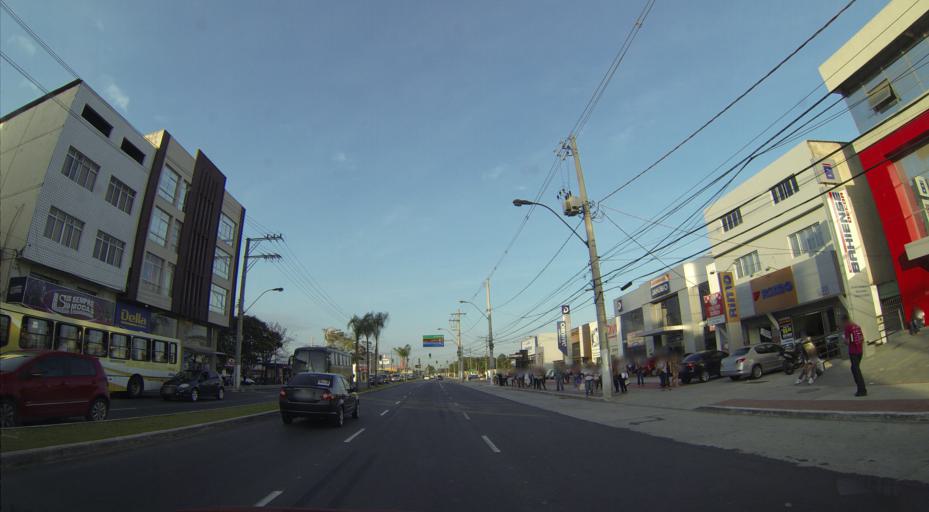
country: BR
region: Espirito Santo
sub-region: Vila Velha
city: Vila Velha
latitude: -20.2668
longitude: -40.2981
